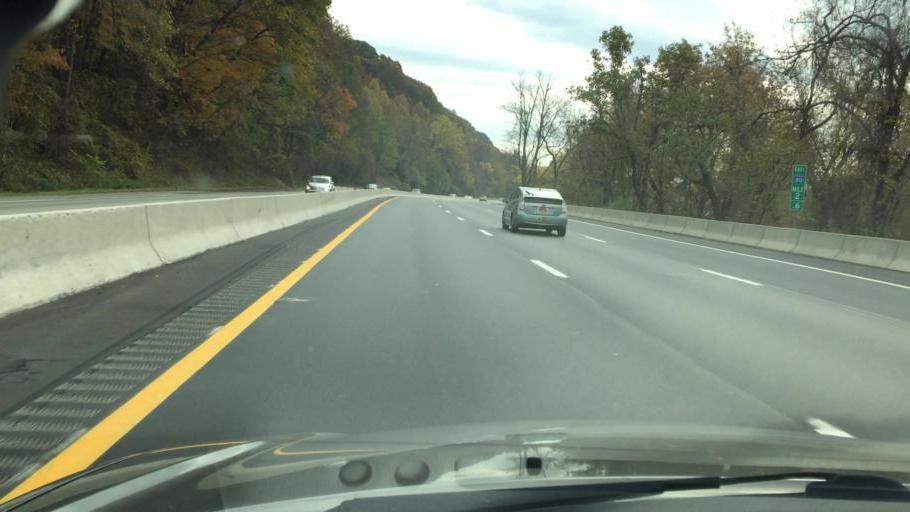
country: US
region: Pennsylvania
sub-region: Monroe County
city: East Stroudsburg
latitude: 40.9501
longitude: -75.1121
